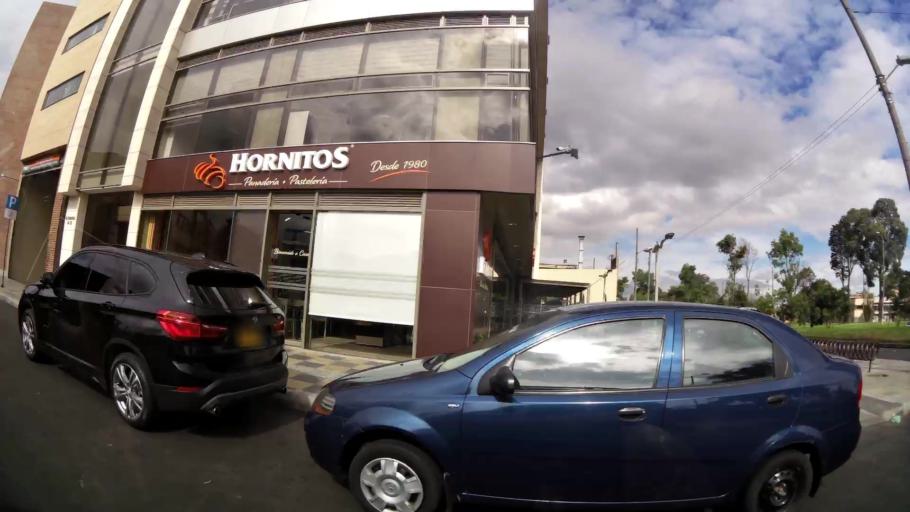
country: CO
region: Bogota D.C.
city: Bogota
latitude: 4.6262
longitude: -74.1012
